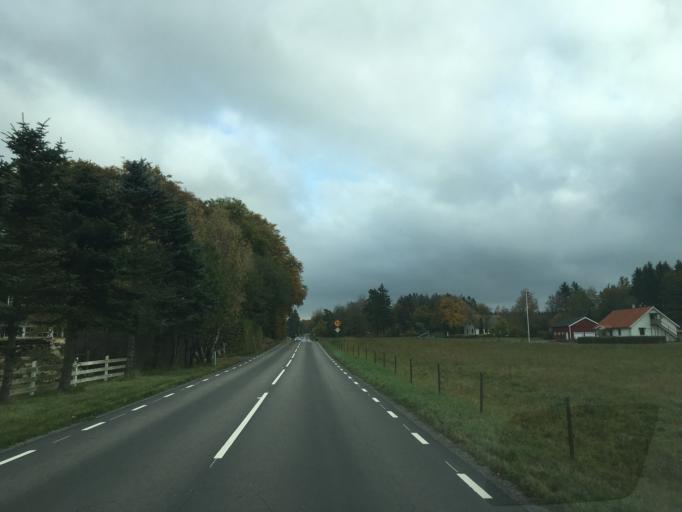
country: SE
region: Skane
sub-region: Tomelilla Kommun
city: Tomelilla
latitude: 55.6375
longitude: 14.0752
